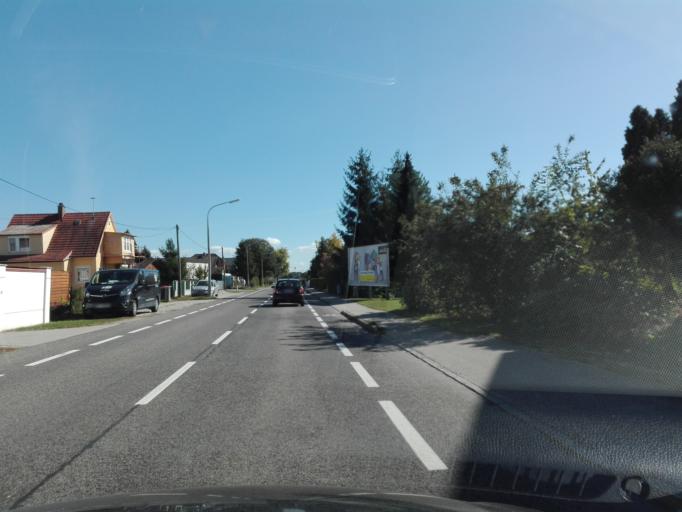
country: AT
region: Lower Austria
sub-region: Politischer Bezirk Amstetten
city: Ennsdorf
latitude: 48.2110
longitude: 14.4923
